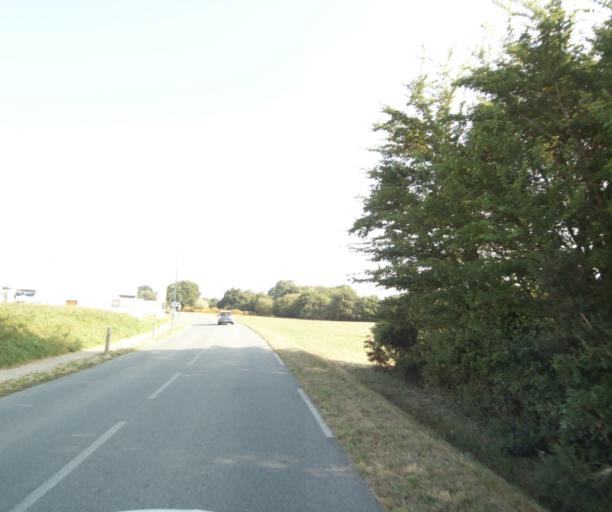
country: FR
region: Brittany
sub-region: Departement du Morbihan
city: Locmiquelic
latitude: 47.7171
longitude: -3.3330
